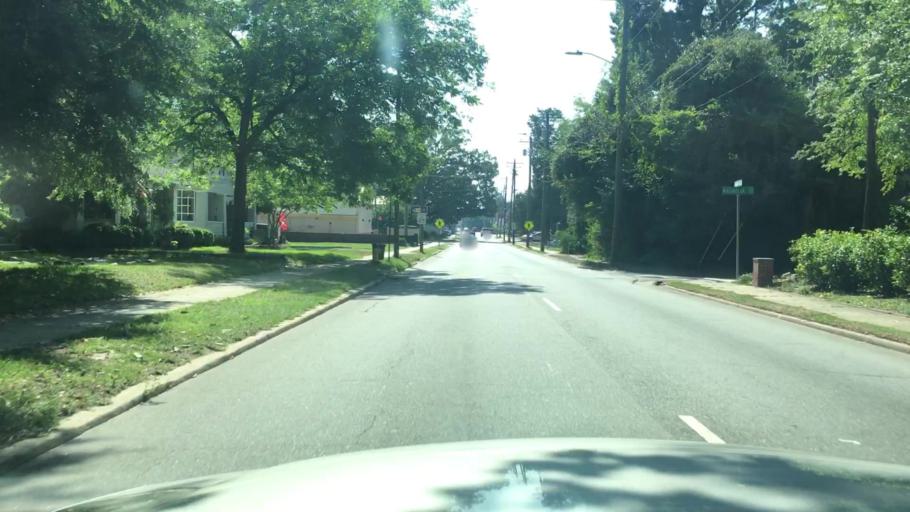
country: US
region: North Carolina
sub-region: Cumberland County
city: Fayetteville
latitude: 35.0577
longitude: -78.9030
